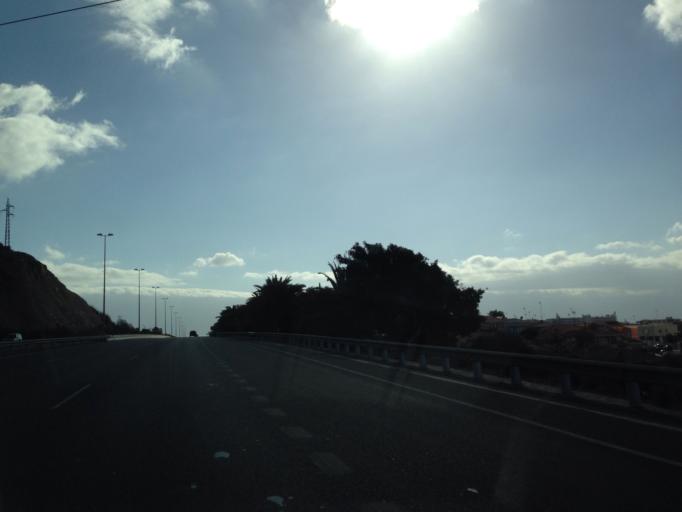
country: ES
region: Canary Islands
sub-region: Provincia de Las Palmas
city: Maspalomas
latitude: 27.7717
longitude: -15.5771
